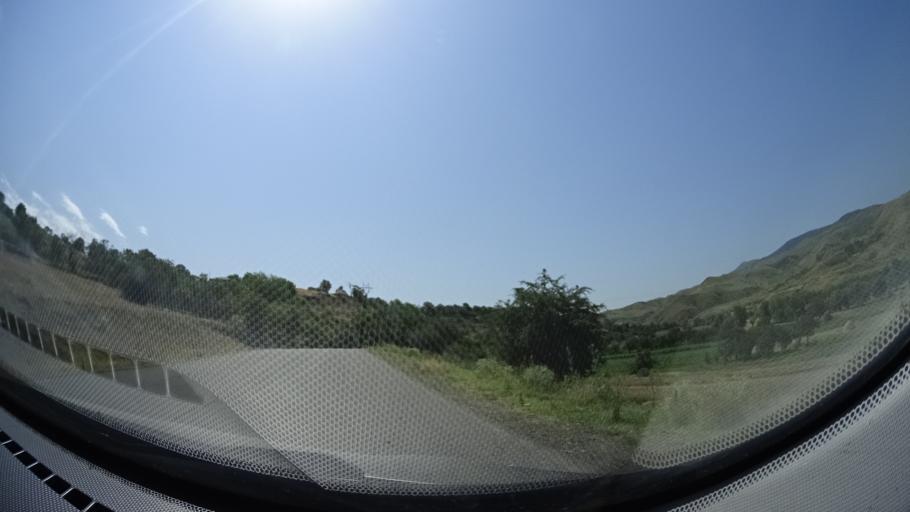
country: GE
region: Samtskhe-Javakheti
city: Aspindza
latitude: 41.5951
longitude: 43.2262
